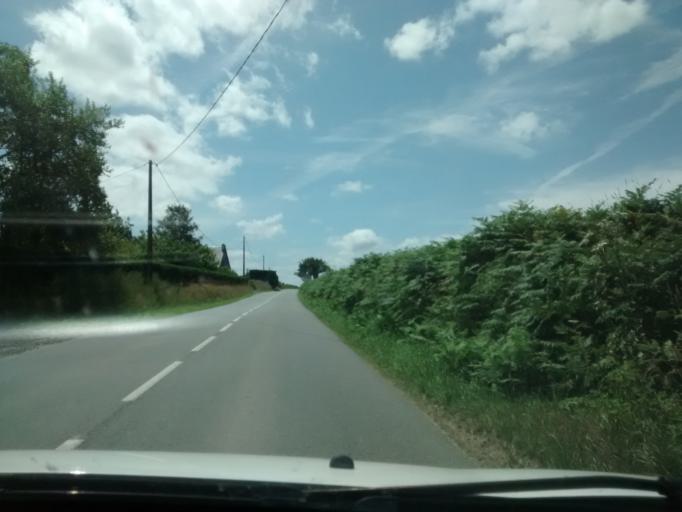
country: FR
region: Brittany
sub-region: Departement des Cotes-d'Armor
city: Penvenan
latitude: 48.8007
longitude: -3.3106
